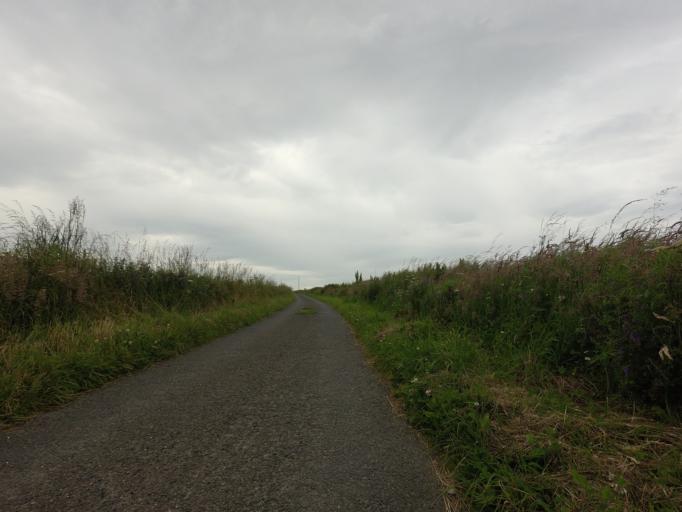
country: GB
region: Scotland
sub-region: Aberdeenshire
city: Whitehills
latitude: 57.6757
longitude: -2.5969
